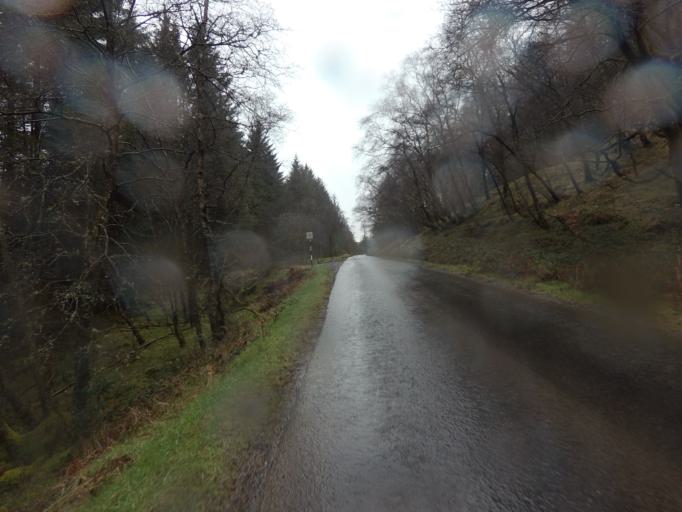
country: GB
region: Scotland
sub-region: West Dunbartonshire
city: Balloch
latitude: 56.2313
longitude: -4.5580
